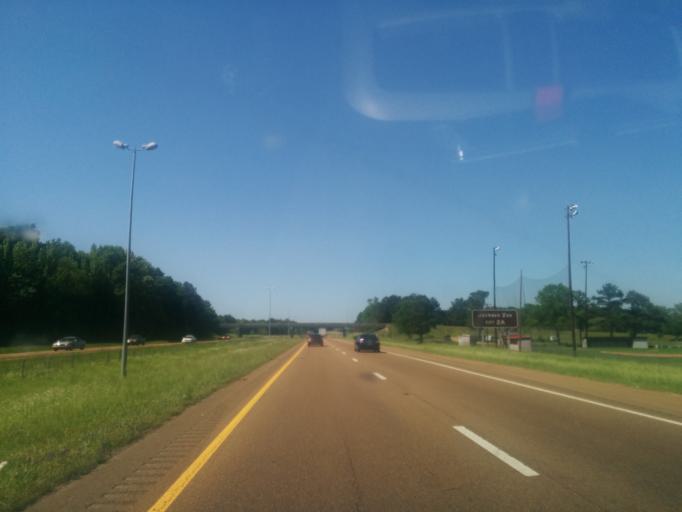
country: US
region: Mississippi
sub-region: Hinds County
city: Jackson
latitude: 32.3169
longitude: -90.2471
